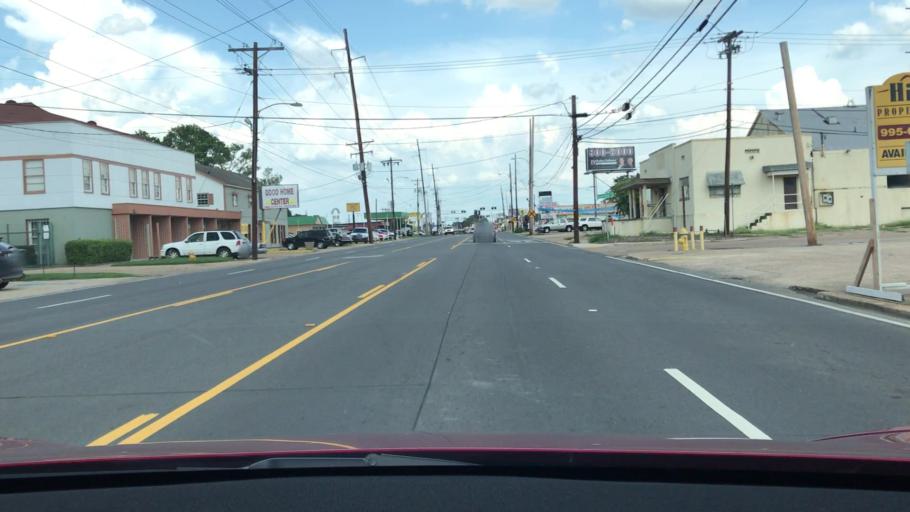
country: US
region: Louisiana
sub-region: Bossier Parish
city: Bossier City
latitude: 32.5158
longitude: -93.7228
